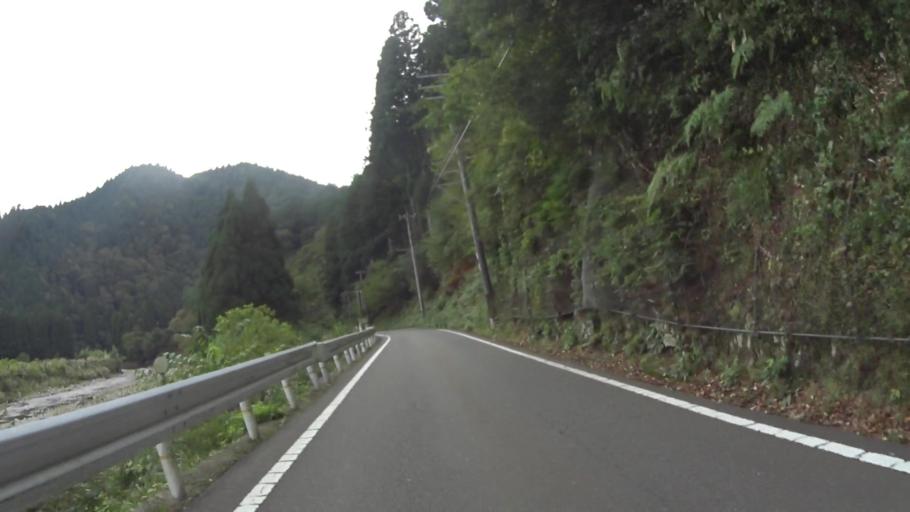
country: JP
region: Fukui
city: Obama
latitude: 35.3185
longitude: 135.6505
